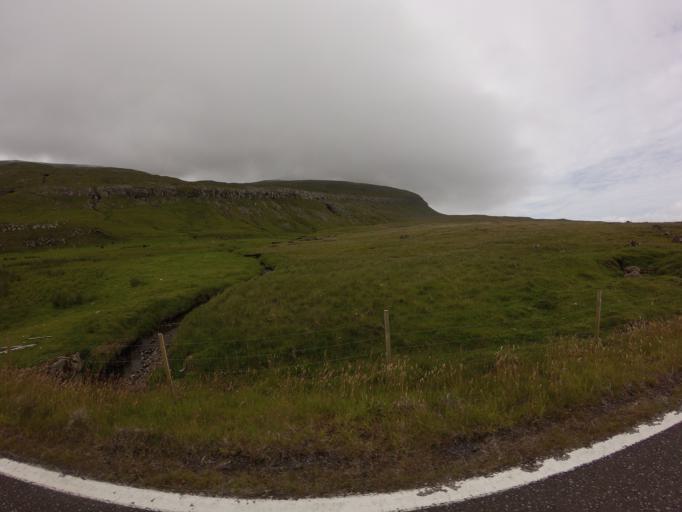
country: FO
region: Sandoy
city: Sandur
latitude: 61.8177
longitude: -6.7160
